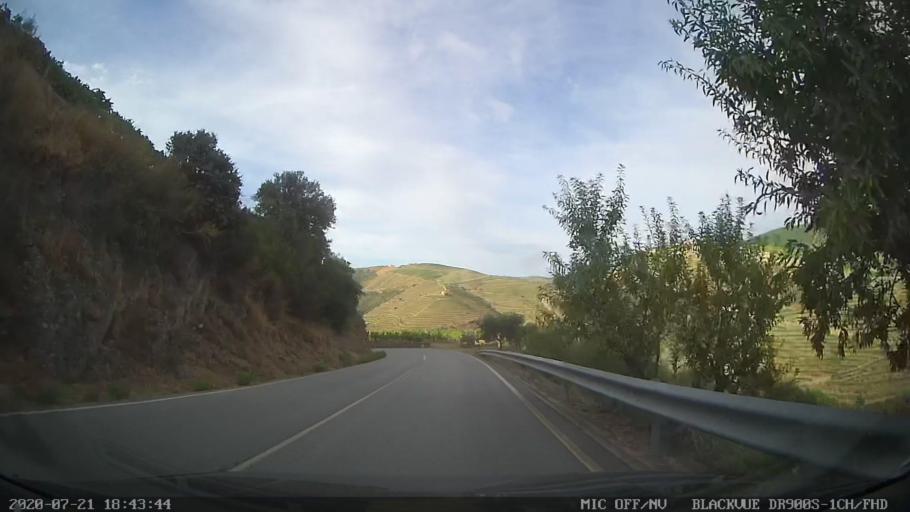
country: PT
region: Viseu
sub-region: Sao Joao da Pesqueira
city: Sao Joao da Pesqueira
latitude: 41.1144
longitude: -7.4573
